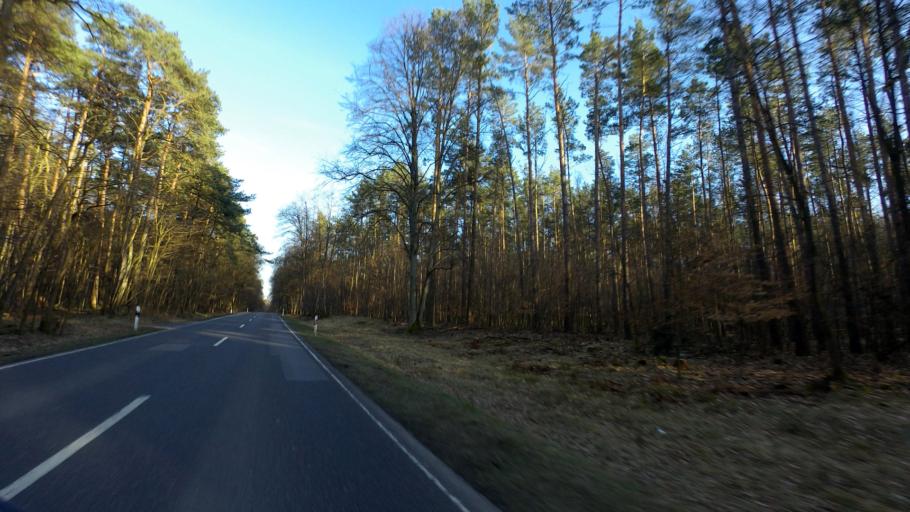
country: DE
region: Brandenburg
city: Joachimsthal
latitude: 52.9525
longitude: 13.7705
